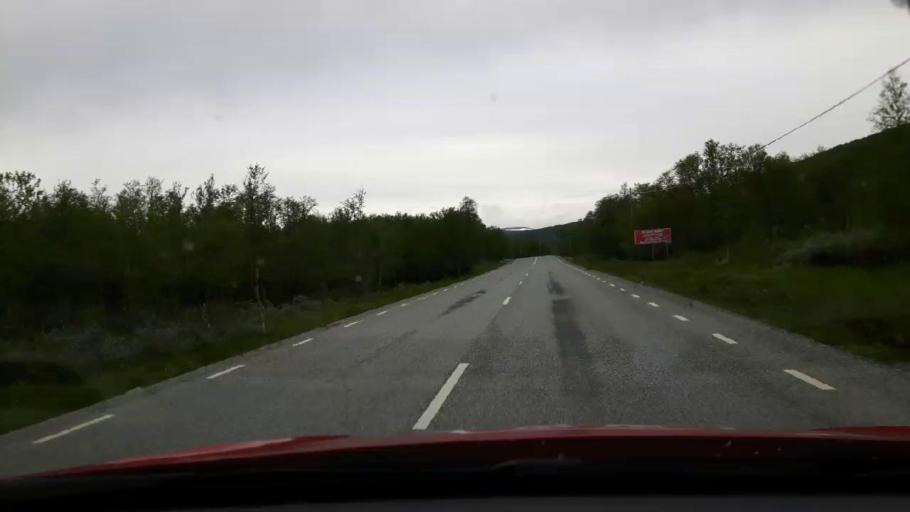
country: NO
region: Sor-Trondelag
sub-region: Tydal
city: Aas
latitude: 62.6913
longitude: 12.4091
